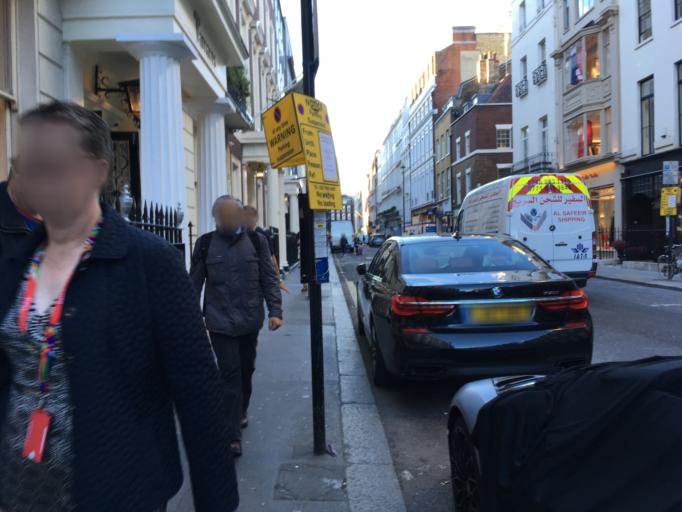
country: GB
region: England
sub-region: Greater London
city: London
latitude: 51.5081
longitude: -0.1418
